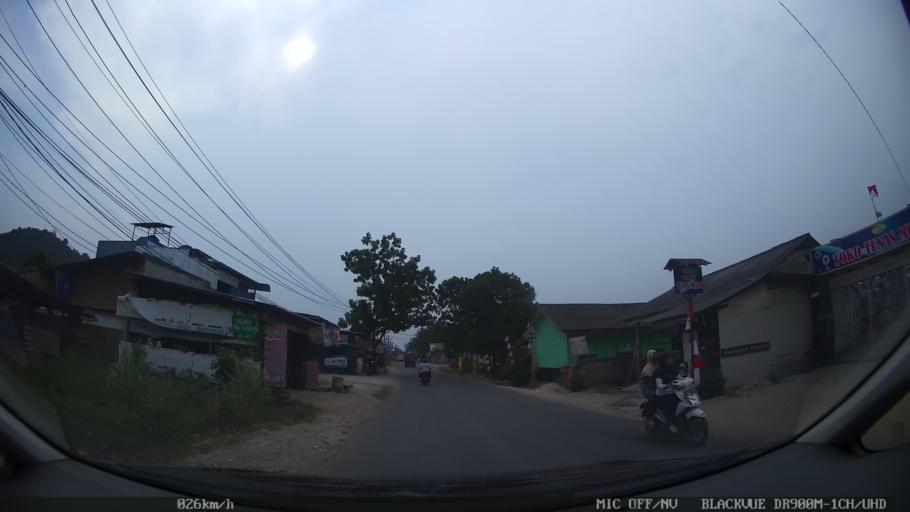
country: ID
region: Lampung
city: Panjang
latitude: -5.4174
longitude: 105.3265
